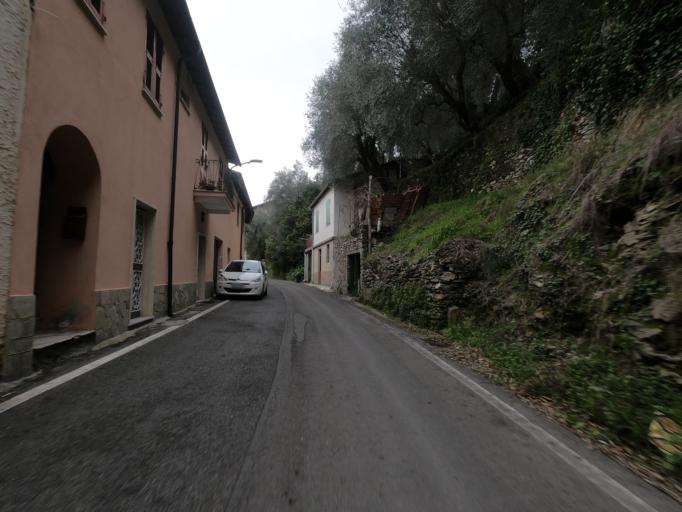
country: IT
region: Liguria
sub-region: Provincia di Savona
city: Casanova Lerrone
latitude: 44.0327
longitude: 8.0244
